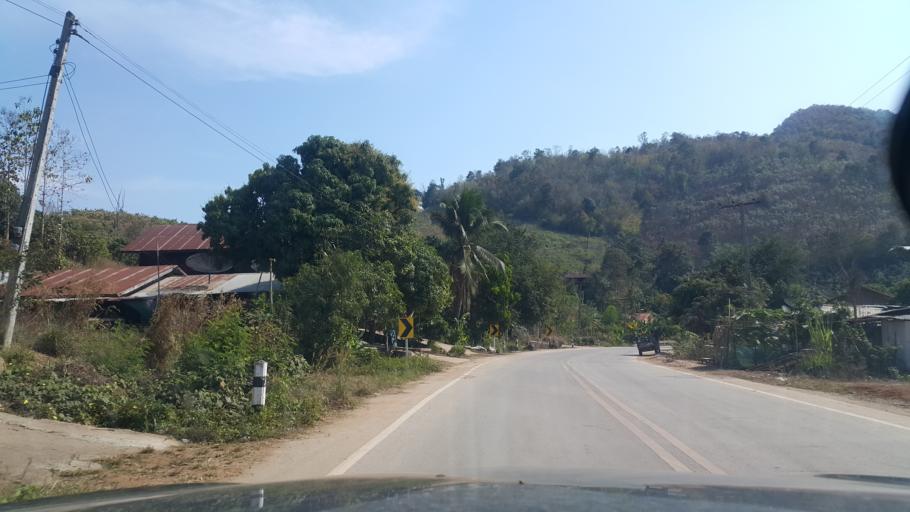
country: TH
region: Loei
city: Pak Chom
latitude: 18.1167
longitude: 101.9987
